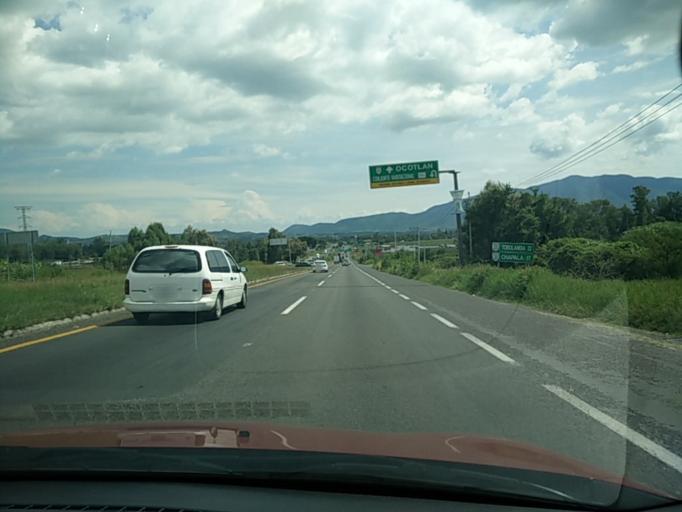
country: MX
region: Jalisco
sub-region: Ixtlahuacan de los Membrillos
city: Los Olivos
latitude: 20.4270
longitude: -103.2389
